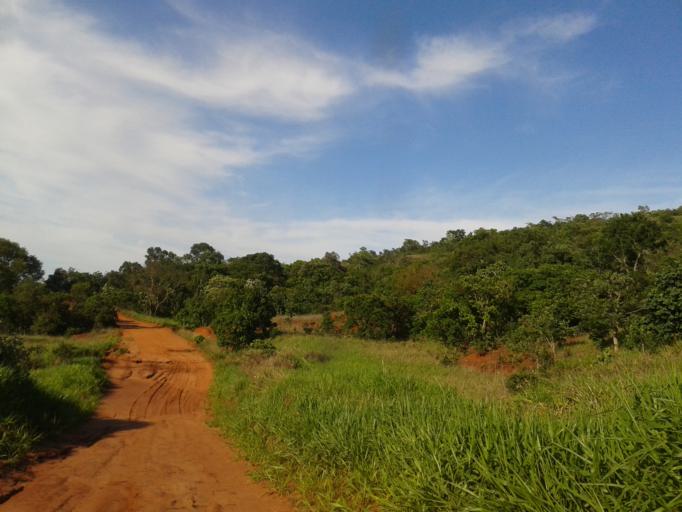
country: BR
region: Minas Gerais
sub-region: Santa Vitoria
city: Santa Vitoria
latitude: -19.1187
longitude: -49.9957
